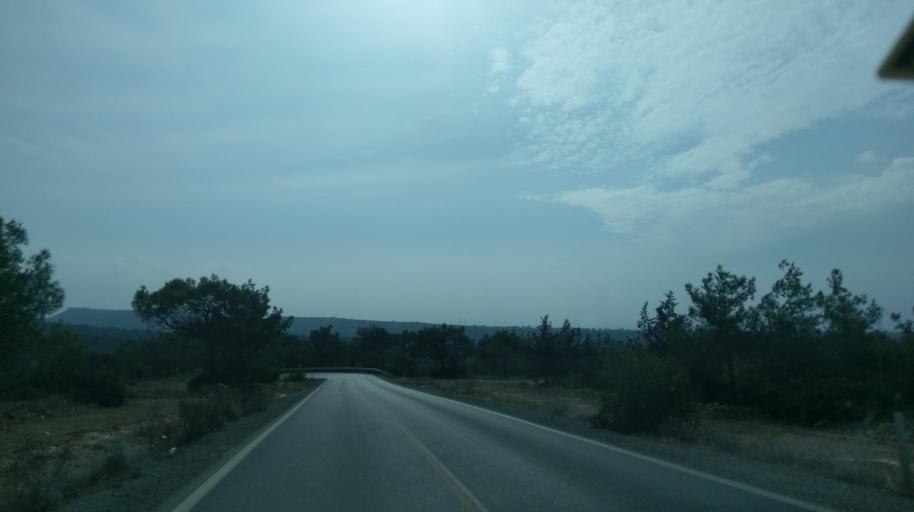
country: CY
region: Lefkosia
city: Morfou
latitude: 35.2706
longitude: 33.0401
